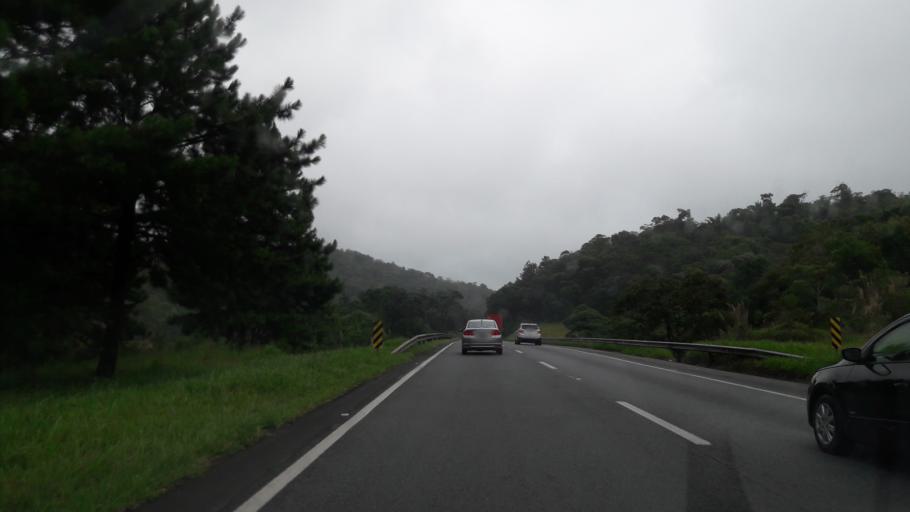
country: BR
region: Parana
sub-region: Campina Grande Do Sul
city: Campina Grande do Sul
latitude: -25.1059
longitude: -48.8062
